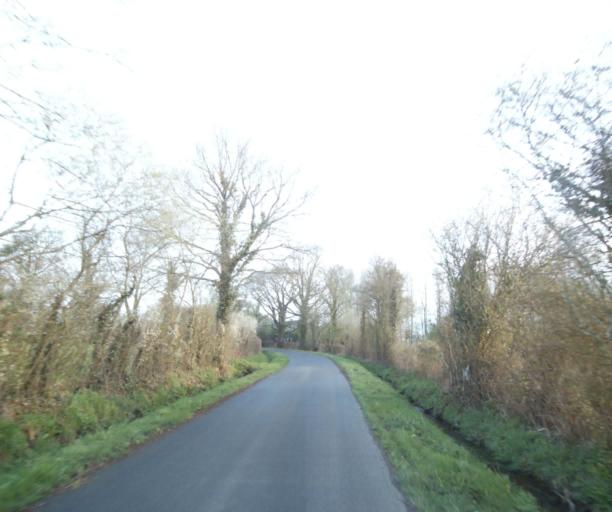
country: FR
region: Pays de la Loire
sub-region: Departement de la Loire-Atlantique
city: Savenay
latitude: 47.3938
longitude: -1.9138
